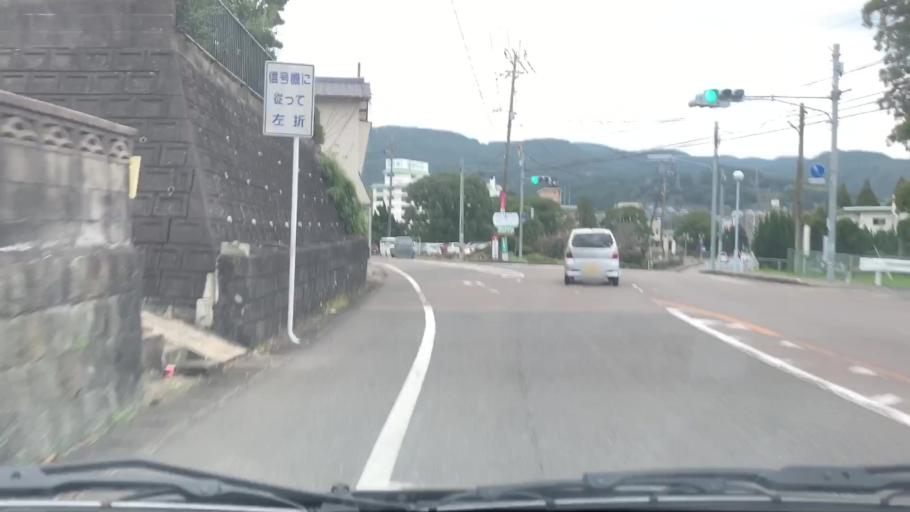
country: JP
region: Saga Prefecture
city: Ureshinomachi-shimojuku
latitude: 33.1004
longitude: 129.9794
